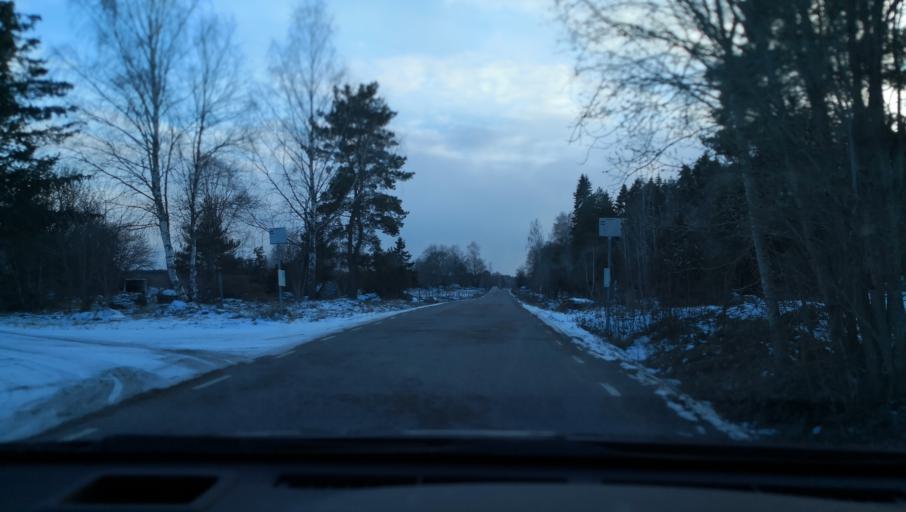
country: SE
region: Vaestmanland
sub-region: Vasteras
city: Tillberga
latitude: 59.6481
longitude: 16.7487
